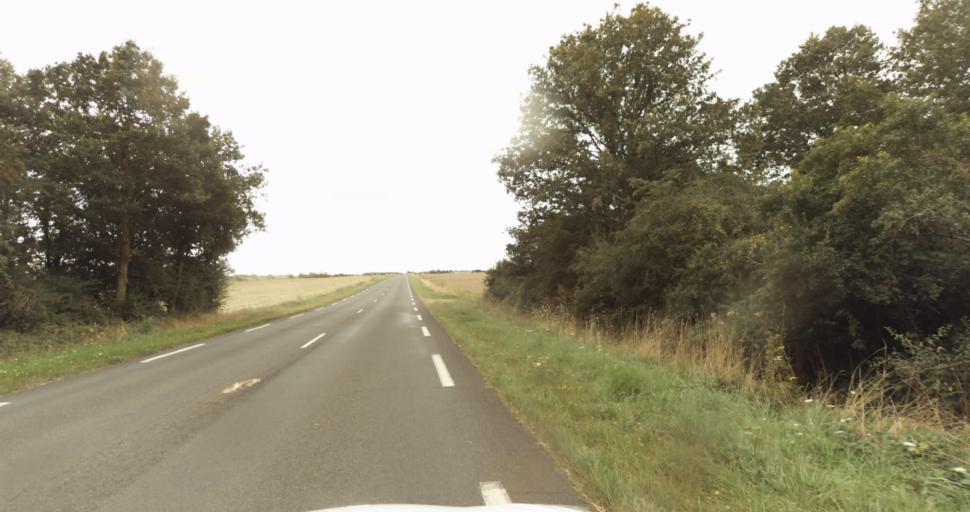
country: FR
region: Haute-Normandie
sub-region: Departement de l'Eure
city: La Madeleine-de-Nonancourt
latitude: 48.8058
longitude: 1.1890
